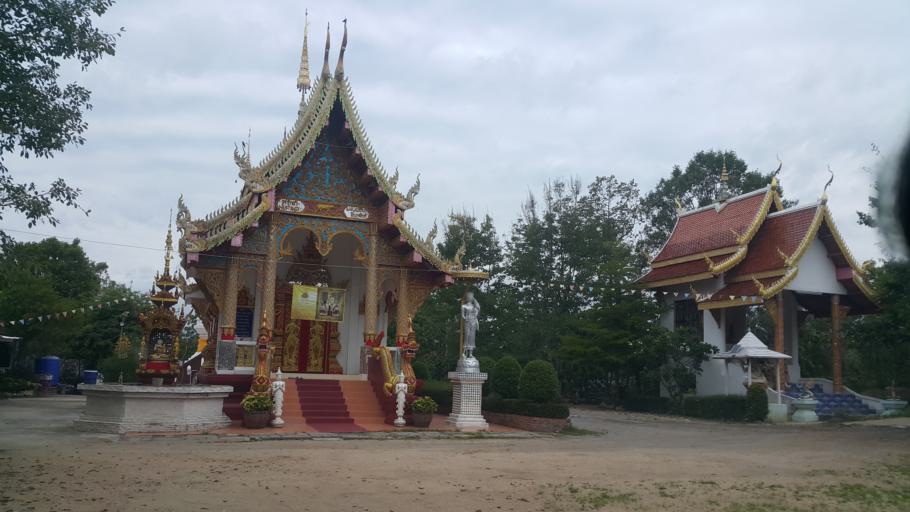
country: TH
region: Chiang Mai
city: San Pa Tong
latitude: 18.6744
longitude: 98.8322
